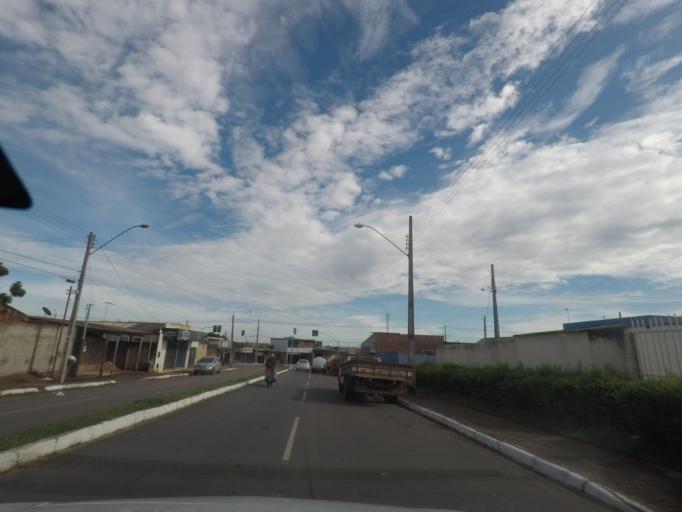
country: BR
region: Goias
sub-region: Aparecida De Goiania
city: Aparecida de Goiania
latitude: -16.8165
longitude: -49.3130
